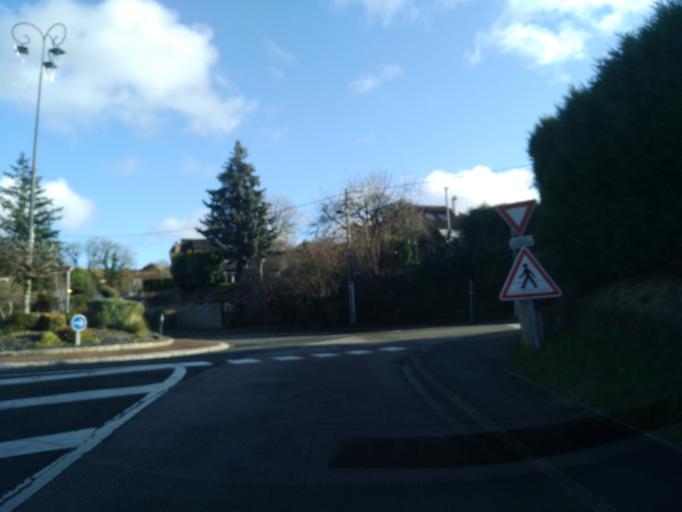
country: FR
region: Ile-de-France
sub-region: Departement des Yvelines
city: Villiers-Saint-Frederic
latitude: 48.8179
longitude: 1.8855
